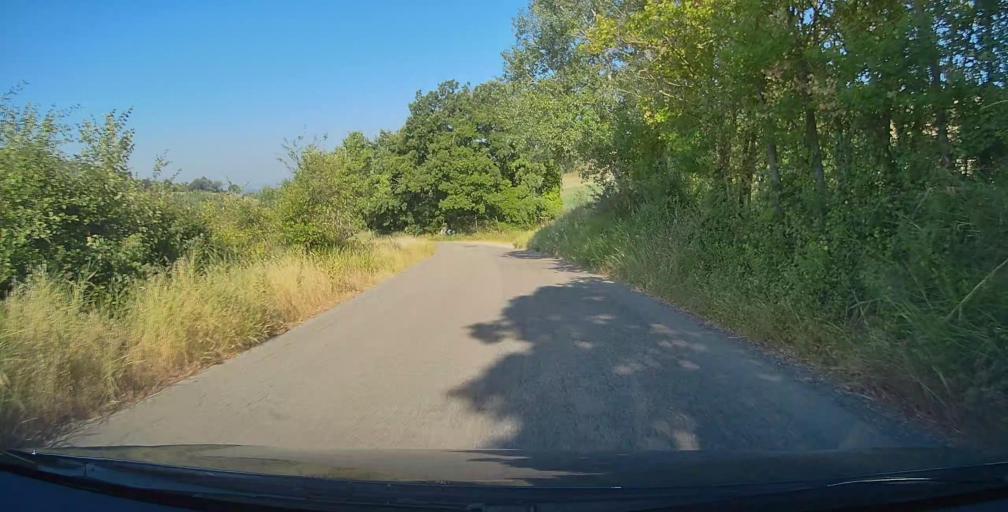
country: IT
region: Umbria
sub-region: Provincia di Terni
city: Otricoli
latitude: 42.4000
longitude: 12.4887
